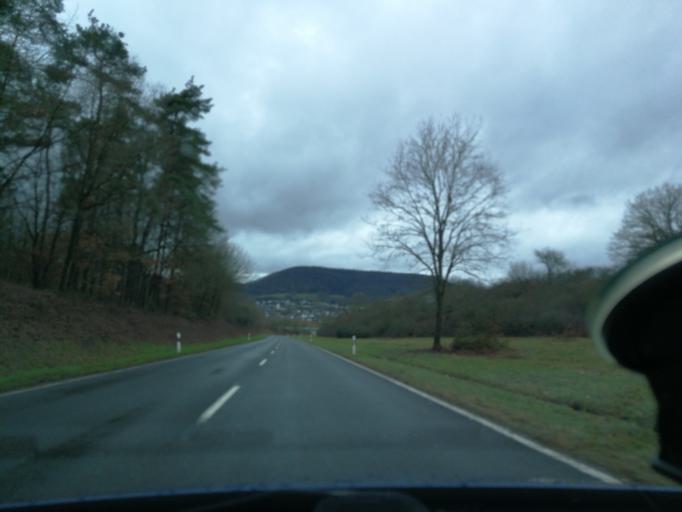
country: DE
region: Rheinland-Pfalz
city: Salmtal
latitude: 49.9197
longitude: 6.8647
